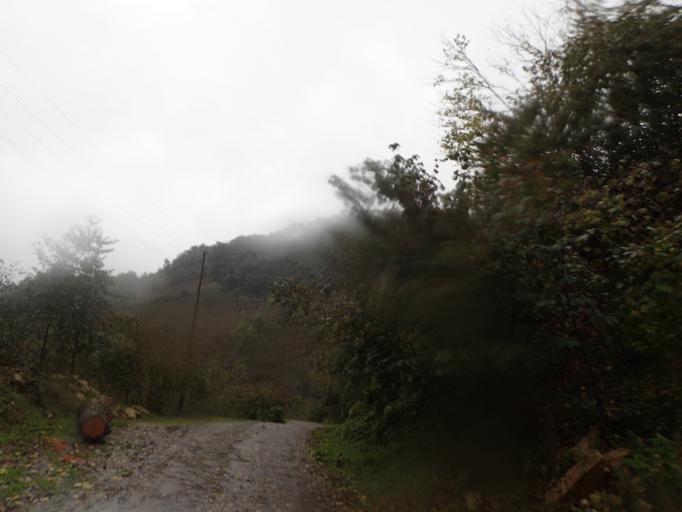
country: TR
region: Ordu
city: Persembe
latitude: 41.0357
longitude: 37.7309
